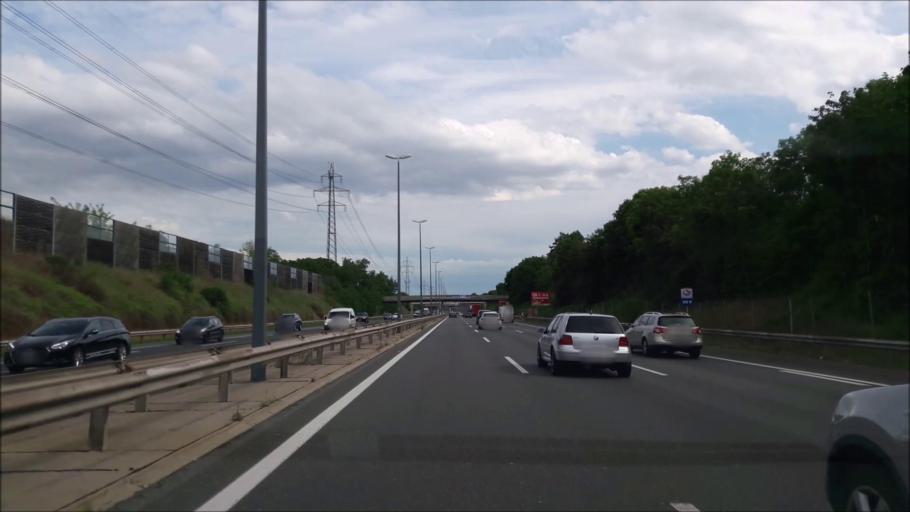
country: AT
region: Lower Austria
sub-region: Politischer Bezirk Korneuburg
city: Langenzersdorf
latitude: 48.2768
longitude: 16.3689
